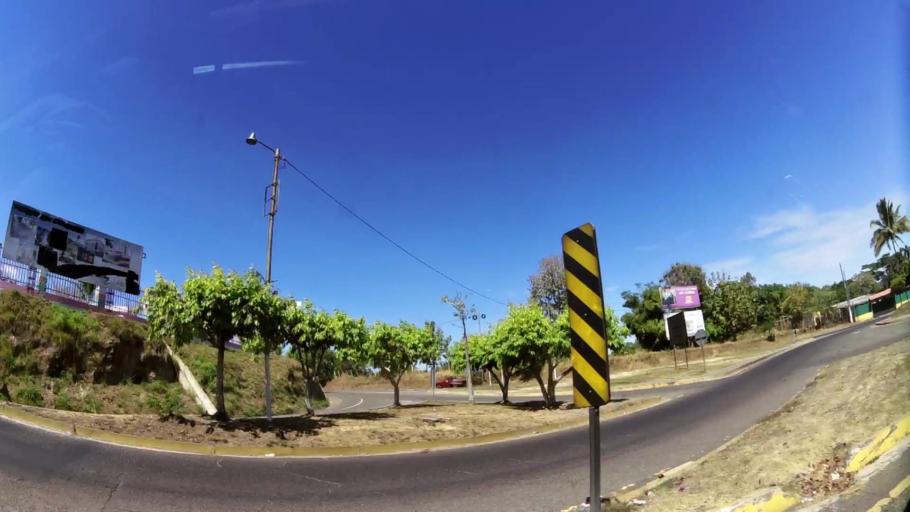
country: SV
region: Ahuachapan
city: Ahuachapan
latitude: 13.9504
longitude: -89.8164
